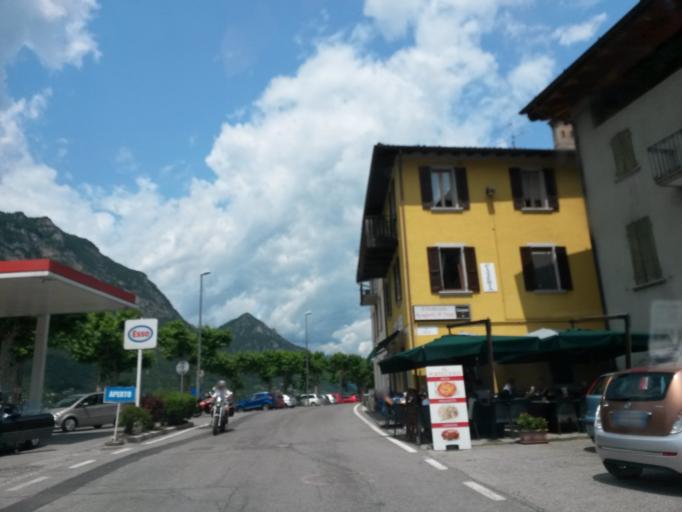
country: IT
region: Lombardy
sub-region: Provincia di Brescia
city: Crone
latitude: 45.7408
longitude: 10.4808
